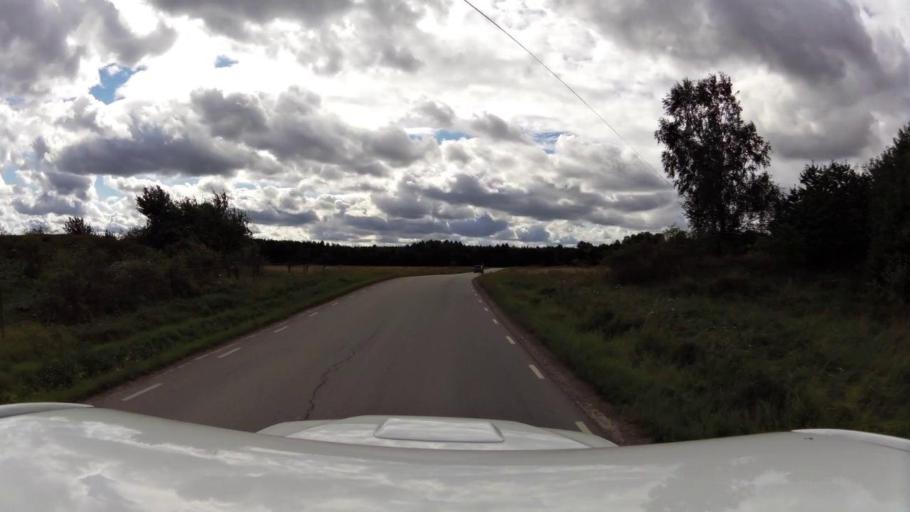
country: SE
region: OEstergoetland
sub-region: Linkopings Kommun
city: Linkoping
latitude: 58.3727
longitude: 15.5865
